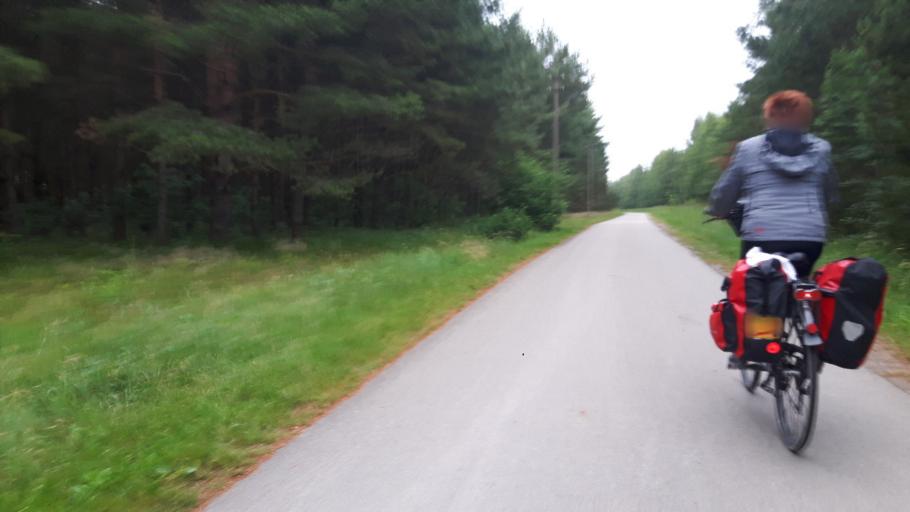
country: LT
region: Klaipedos apskritis
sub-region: Palanga
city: Sventoji
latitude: 55.9925
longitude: 21.0752
